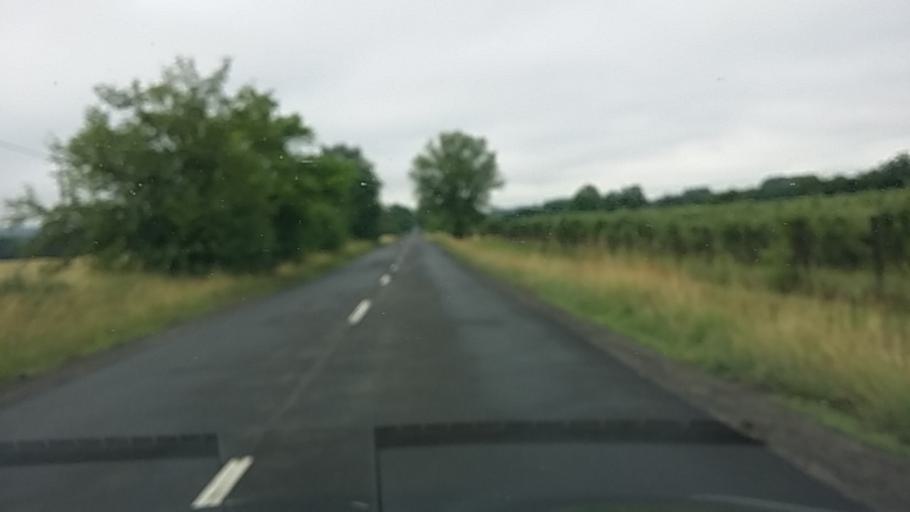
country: SK
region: Nitriansky
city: Zeliezovce
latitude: 47.9668
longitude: 18.7825
